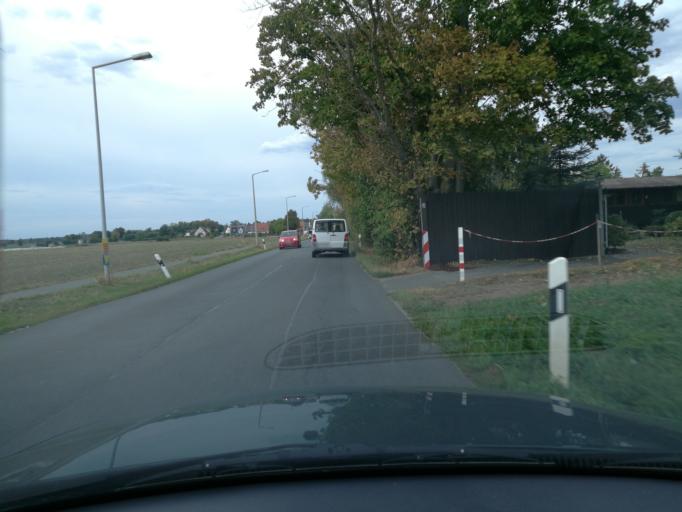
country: DE
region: Bavaria
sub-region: Regierungsbezirk Mittelfranken
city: Wetzendorf
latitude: 49.5052
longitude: 11.0467
